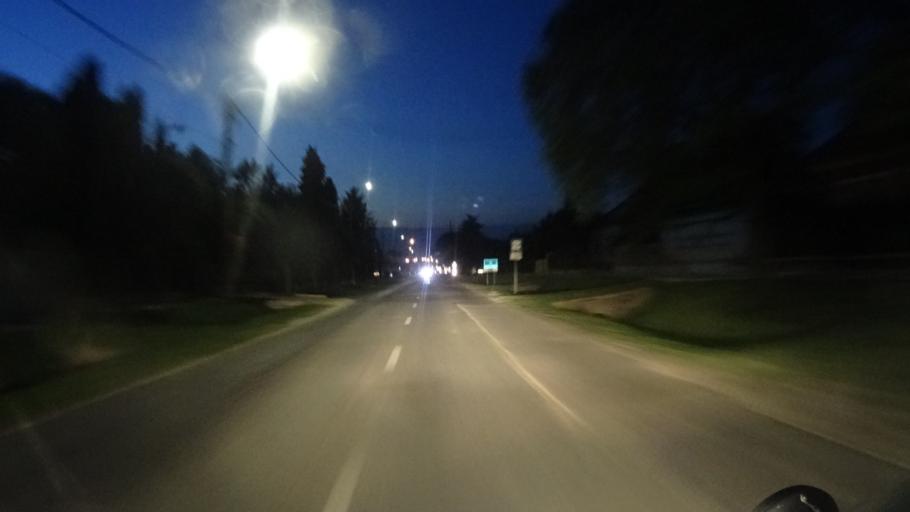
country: HU
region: Somogy
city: Balatonbereny
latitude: 46.7013
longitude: 17.3700
